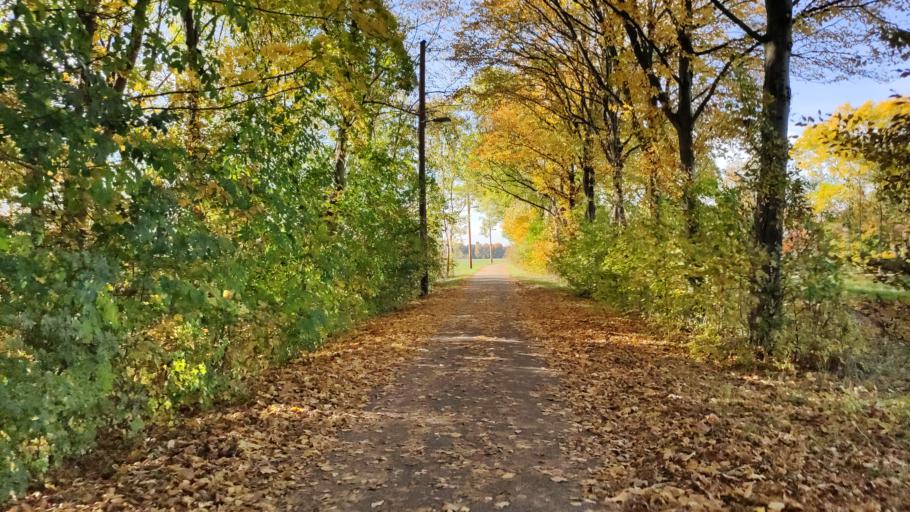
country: DE
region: Bavaria
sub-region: Upper Bavaria
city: Pasing
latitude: 48.1329
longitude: 11.4752
